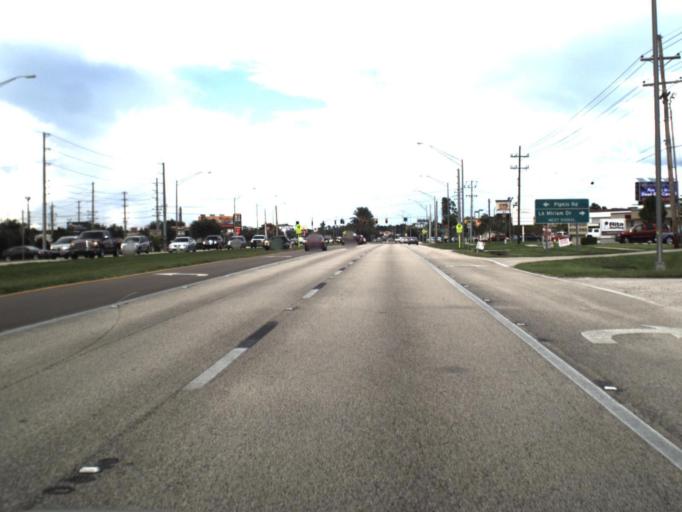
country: US
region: Florida
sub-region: Polk County
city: Medulla
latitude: 27.9726
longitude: -81.9614
